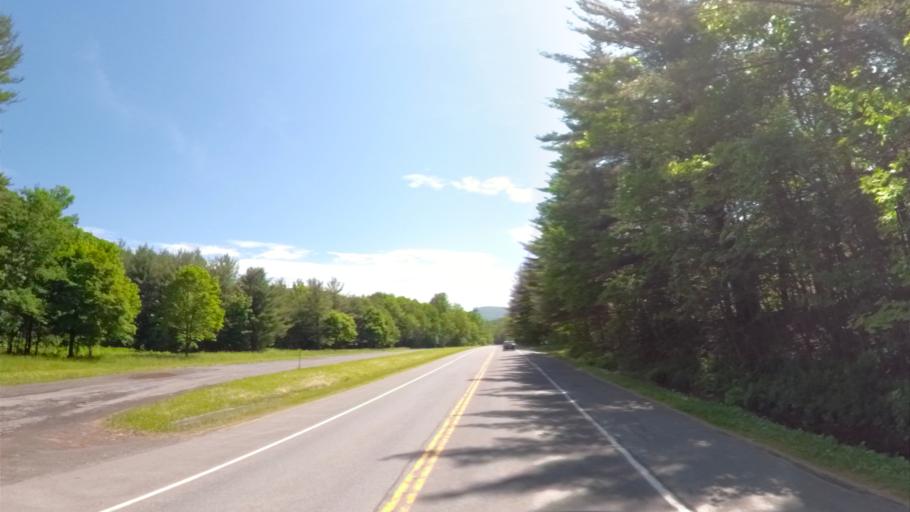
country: US
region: New York
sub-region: Ulster County
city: Shokan
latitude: 42.1154
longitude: -74.4139
